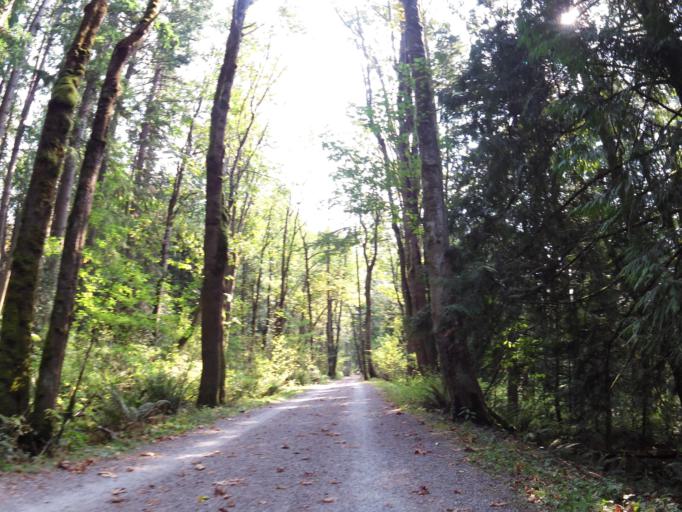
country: US
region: Washington
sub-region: Whatcom County
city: Bellingham
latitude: 48.7052
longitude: -122.4859
